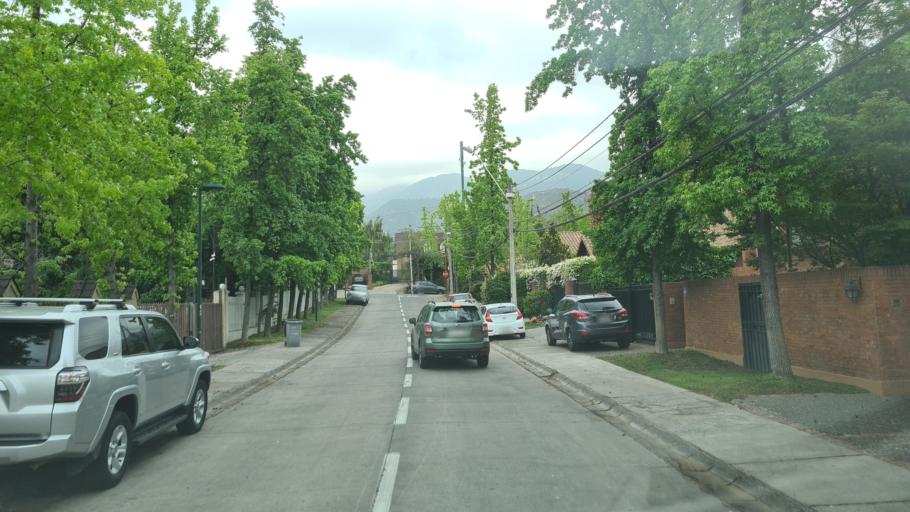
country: CL
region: Santiago Metropolitan
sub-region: Provincia de Santiago
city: Villa Presidente Frei, Nunoa, Santiago, Chile
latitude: -33.3390
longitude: -70.5060
